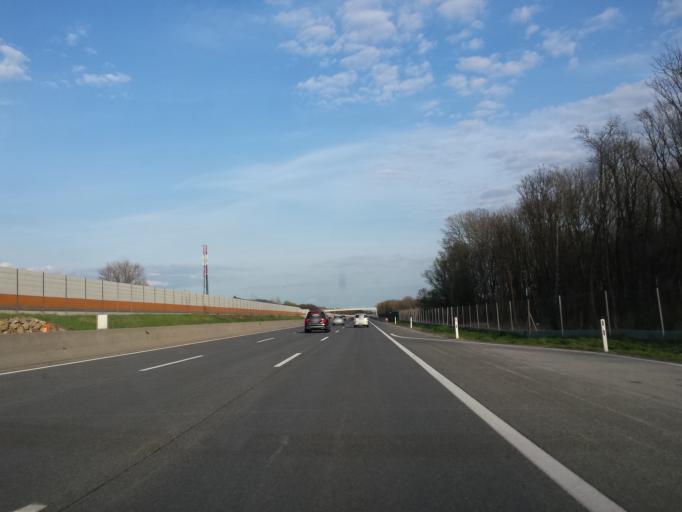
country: AT
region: Lower Austria
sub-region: Politischer Bezirk Korneuburg
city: Spillern
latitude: 48.3738
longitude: 16.2675
